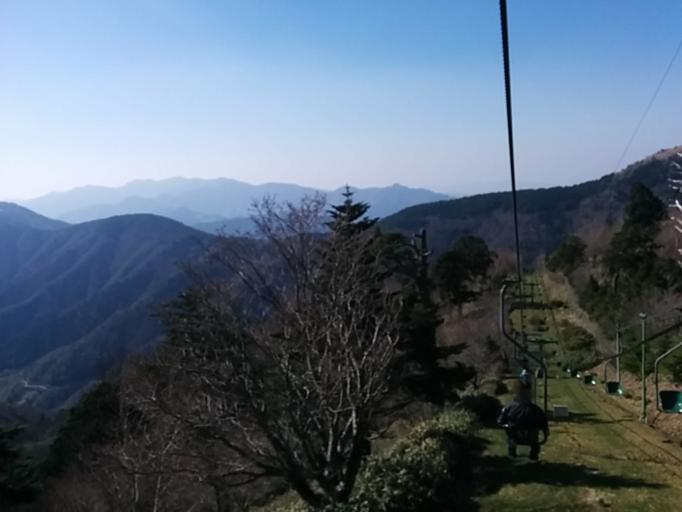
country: JP
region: Tokushima
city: Wakimachi
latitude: 33.8616
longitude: 134.0917
